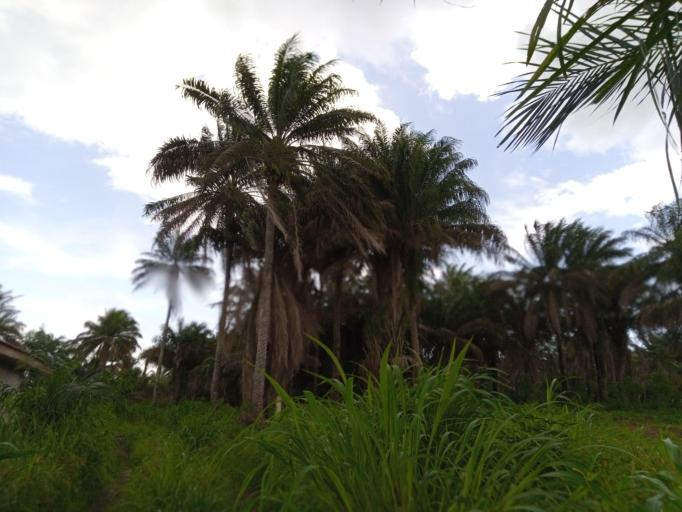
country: SL
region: Northern Province
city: Masoyila
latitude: 8.5821
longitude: -13.1660
